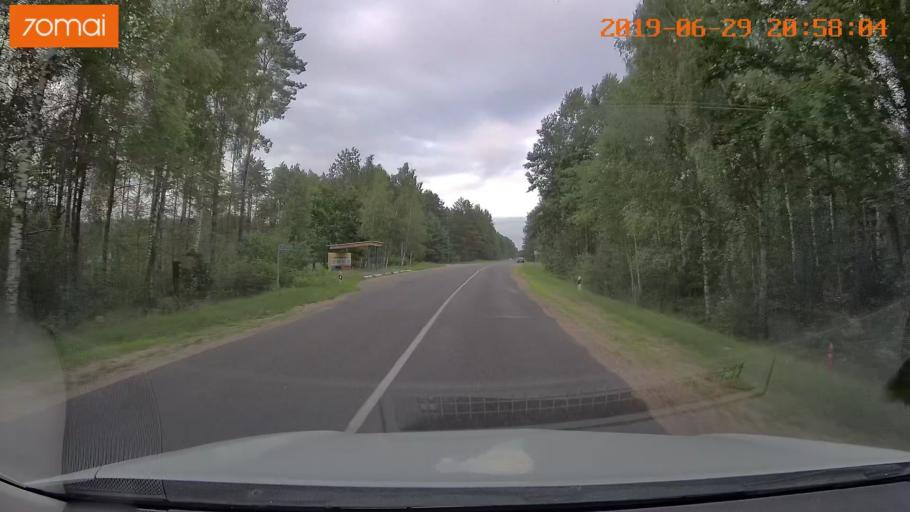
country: BY
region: Brest
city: Hantsavichy
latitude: 52.7266
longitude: 26.3792
